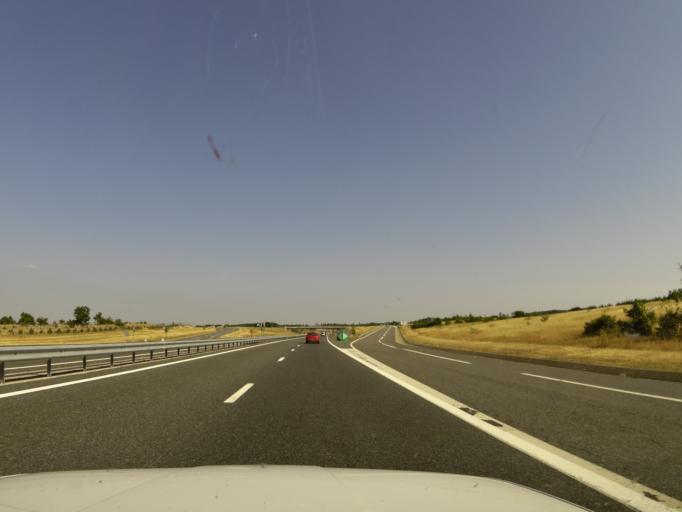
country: FR
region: Midi-Pyrenees
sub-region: Departement de l'Aveyron
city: La Cavalerie
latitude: 44.0148
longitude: 3.1370
